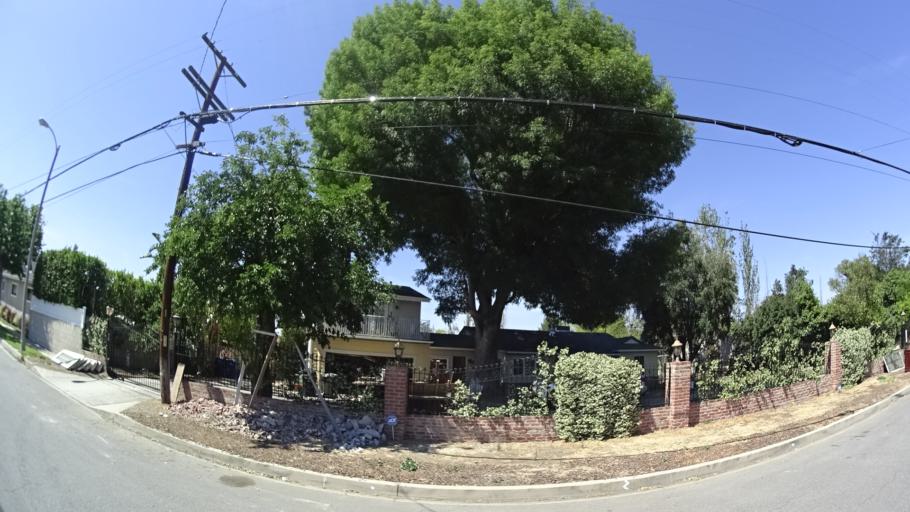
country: US
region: California
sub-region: Los Angeles County
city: Van Nuys
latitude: 34.1739
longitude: -118.4251
